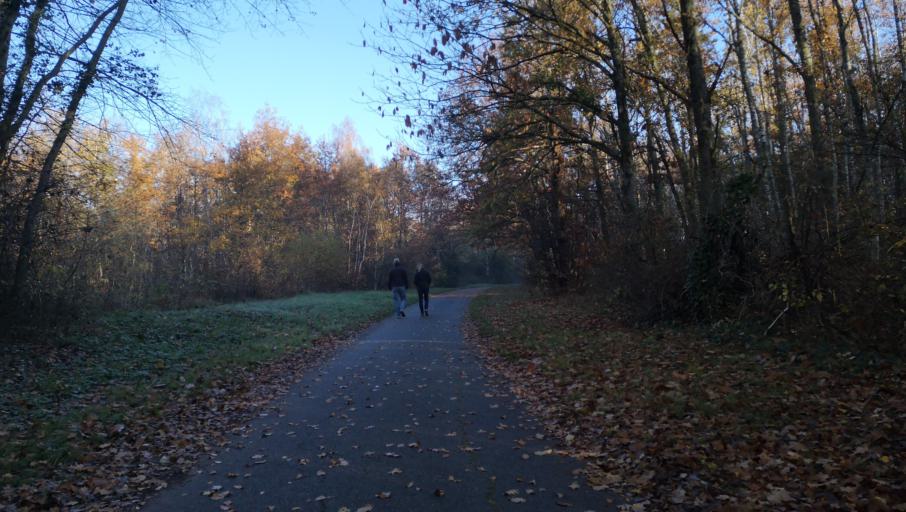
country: FR
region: Centre
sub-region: Departement du Loiret
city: Saran
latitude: 47.9359
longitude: 1.8597
